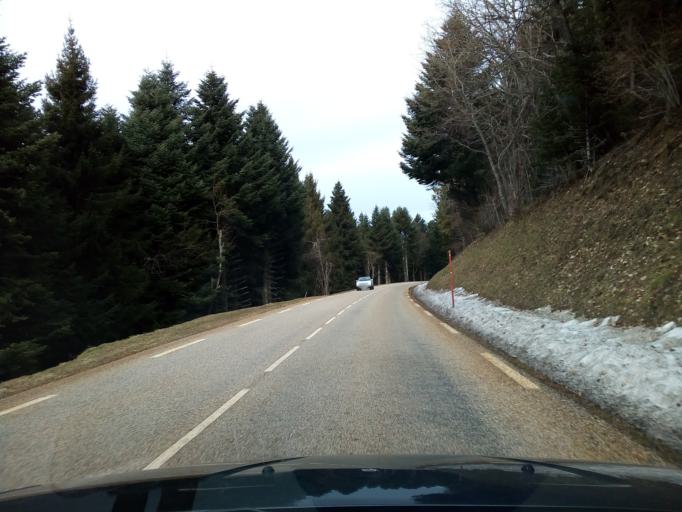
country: FR
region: Rhone-Alpes
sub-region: Departement de l'Isere
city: Revel
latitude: 45.1429
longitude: 5.8743
